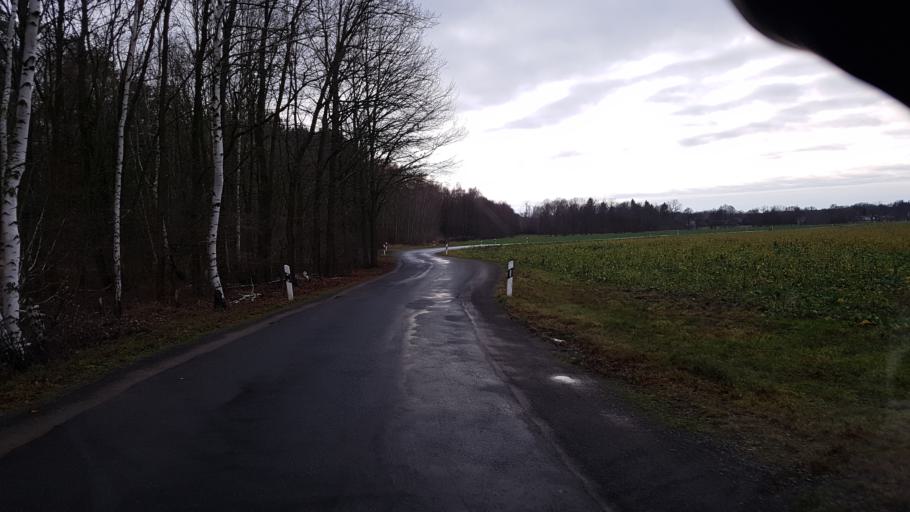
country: DE
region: Brandenburg
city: Altdobern
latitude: 51.6638
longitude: 14.0264
